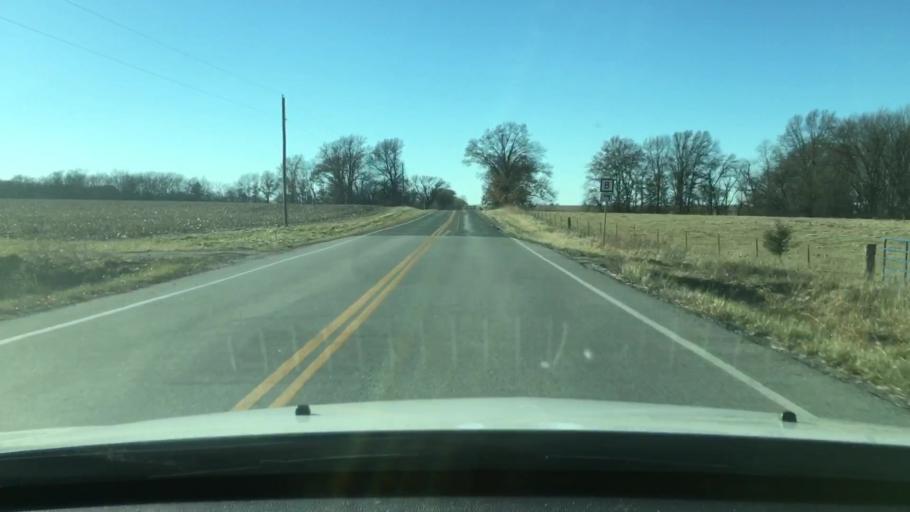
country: US
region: Missouri
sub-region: Audrain County
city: Mexico
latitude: 39.2816
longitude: -91.7164
